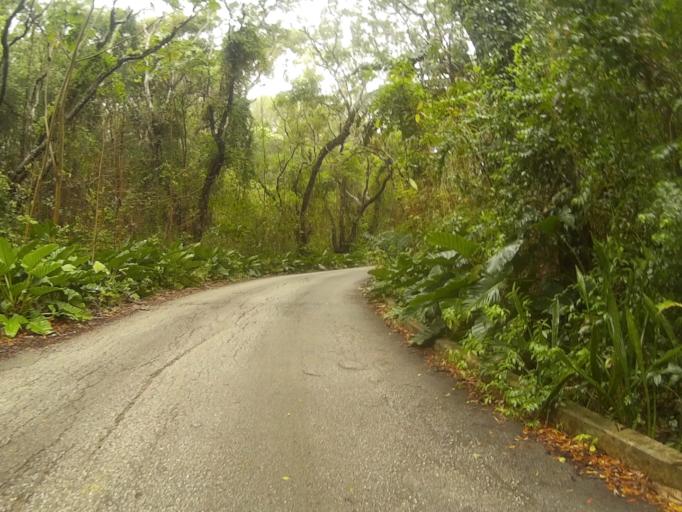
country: BB
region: Saint Andrew
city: Greenland
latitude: 13.2759
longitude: -59.5877
